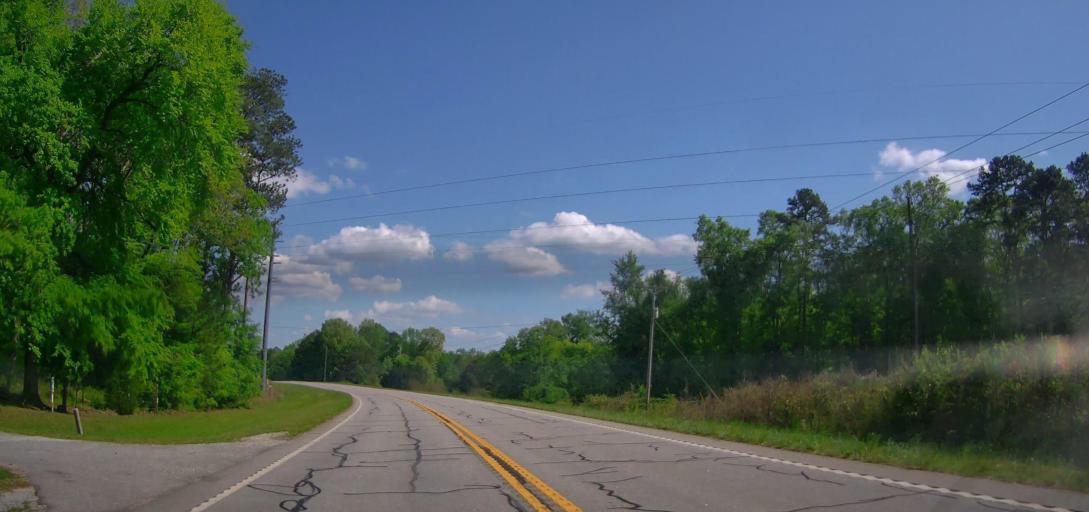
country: US
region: Georgia
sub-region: Greene County
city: Greensboro
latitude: 33.5845
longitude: -83.2819
